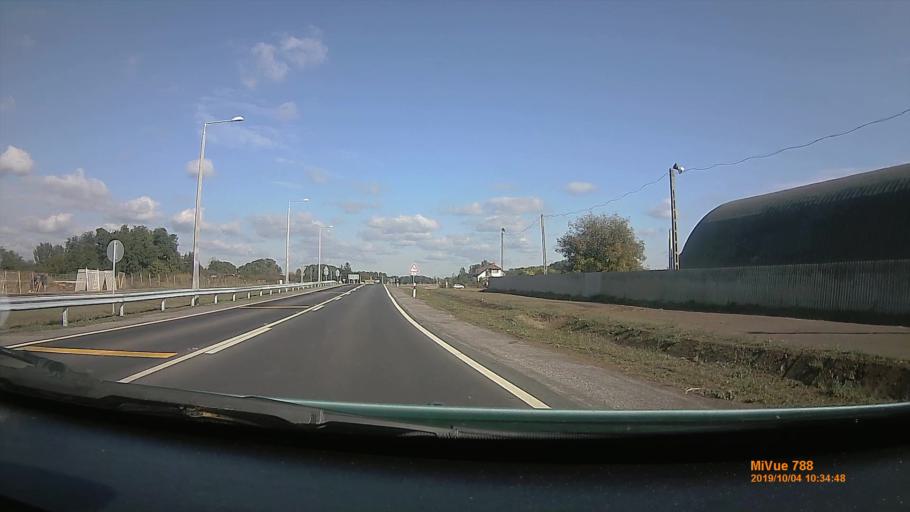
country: HU
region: Szabolcs-Szatmar-Bereg
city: Nyiregyhaza
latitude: 47.9576
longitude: 21.6558
